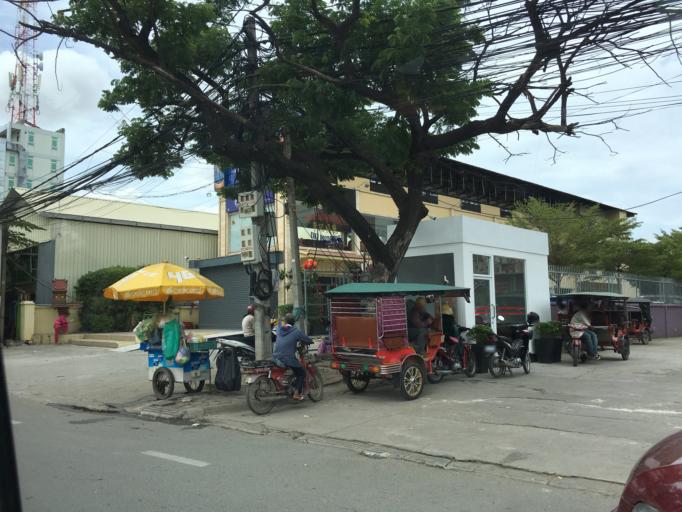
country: KH
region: Phnom Penh
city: Phnom Penh
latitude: 11.5367
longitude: 104.9236
